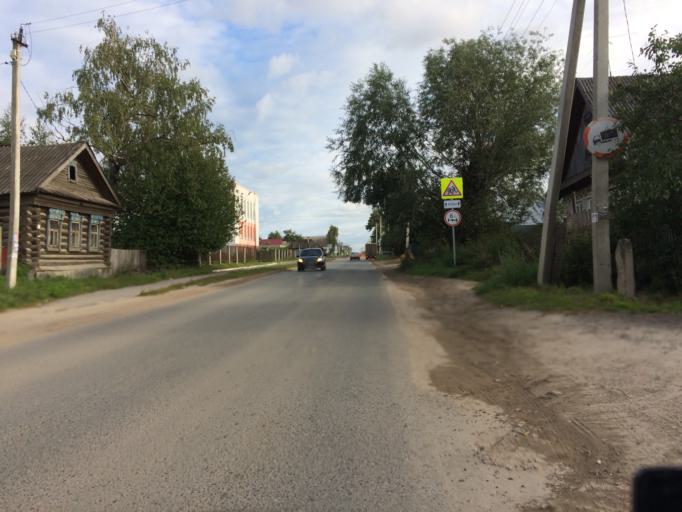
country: RU
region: Mariy-El
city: Yoshkar-Ola
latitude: 56.6477
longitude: 47.9810
